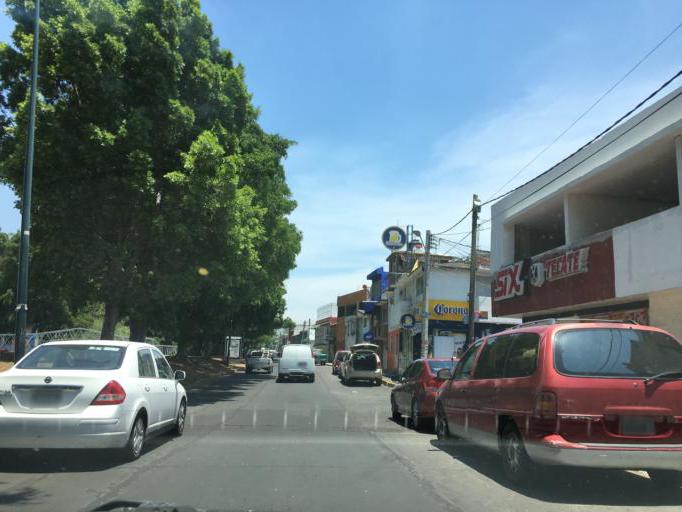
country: MX
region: Michoacan
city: Morelia
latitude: 19.6930
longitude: -101.1992
